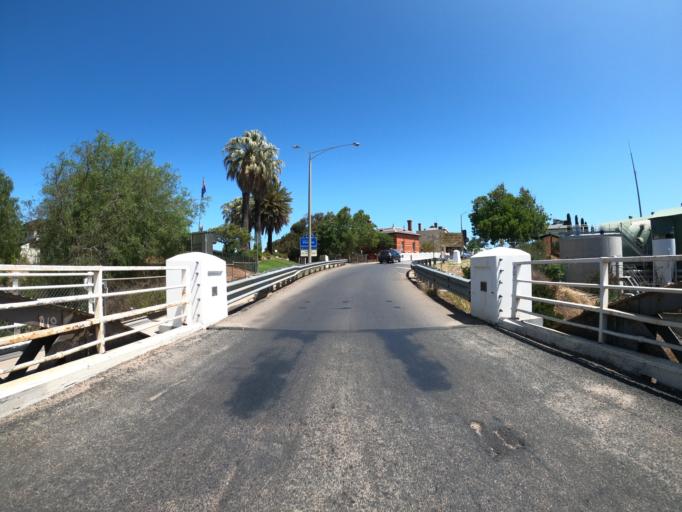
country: AU
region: New South Wales
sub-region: Corowa Shire
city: Corowa
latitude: -36.0073
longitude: 146.3952
